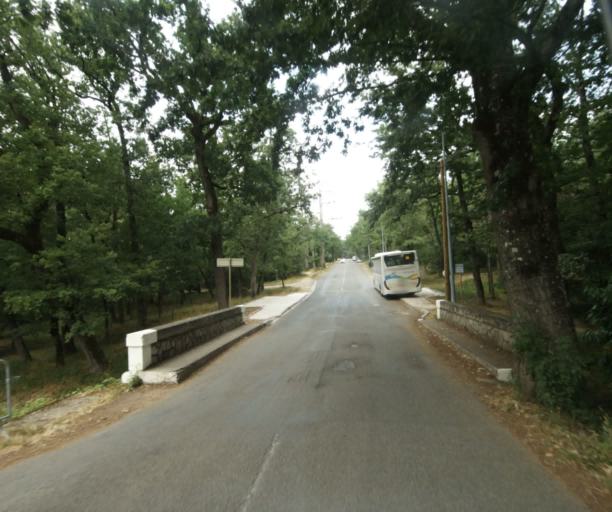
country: FR
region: Midi-Pyrenees
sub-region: Departement de la Haute-Garonne
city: Revel
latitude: 43.4342
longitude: 2.0183
